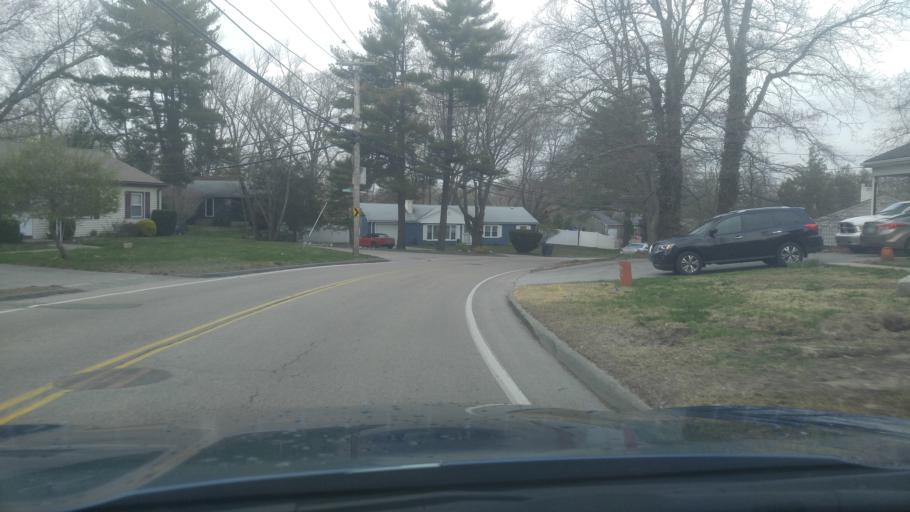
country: US
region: Rhode Island
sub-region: Kent County
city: East Greenwich
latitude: 41.6949
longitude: -71.4695
